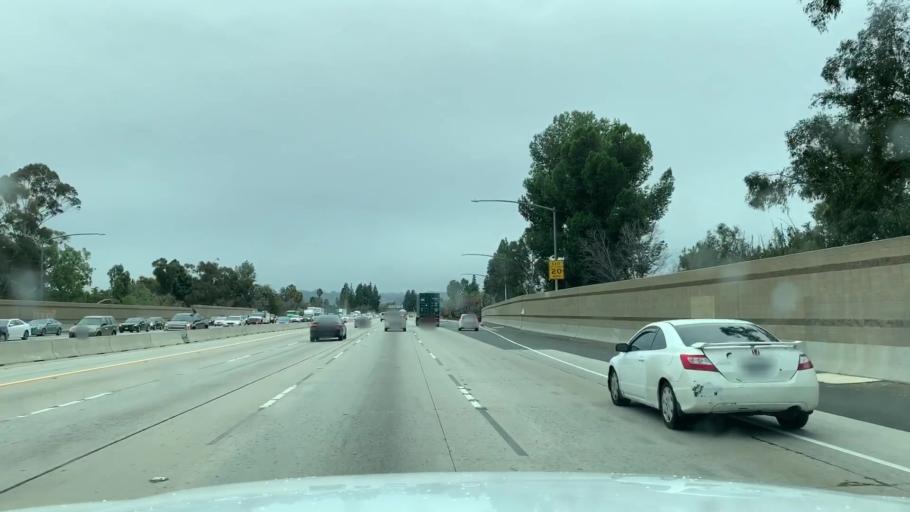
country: US
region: California
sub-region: Los Angeles County
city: Van Nuys
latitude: 34.2054
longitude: -118.4735
